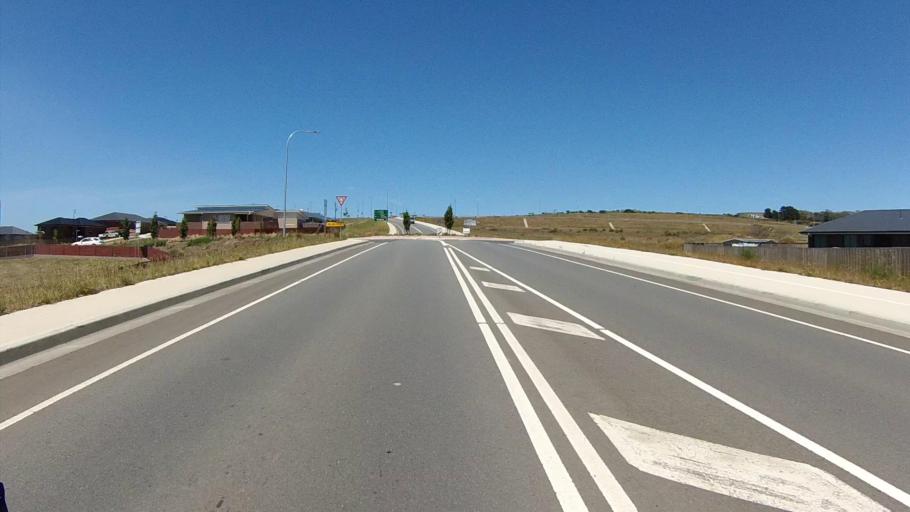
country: AU
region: Tasmania
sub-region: Clarence
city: Howrah
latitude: -42.8859
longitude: 147.4285
